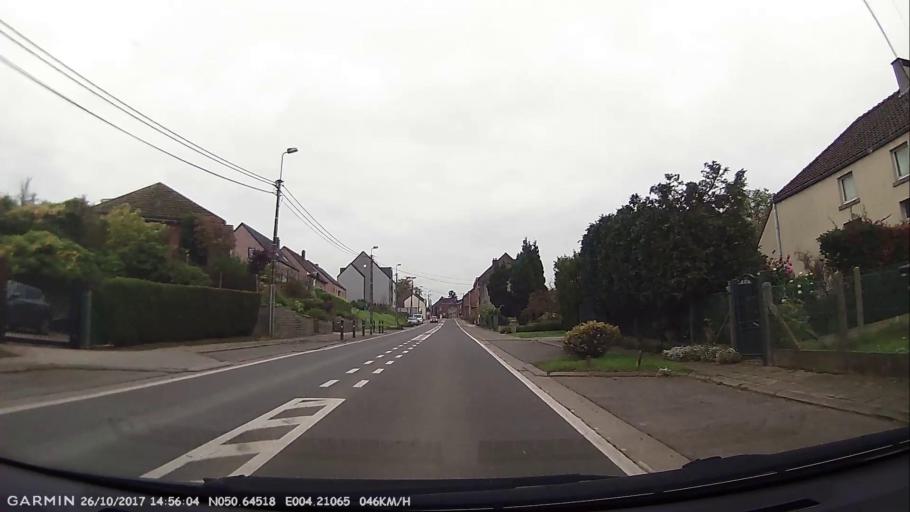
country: BE
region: Wallonia
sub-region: Province du Brabant Wallon
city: Tubize
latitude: 50.6451
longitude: 4.2105
